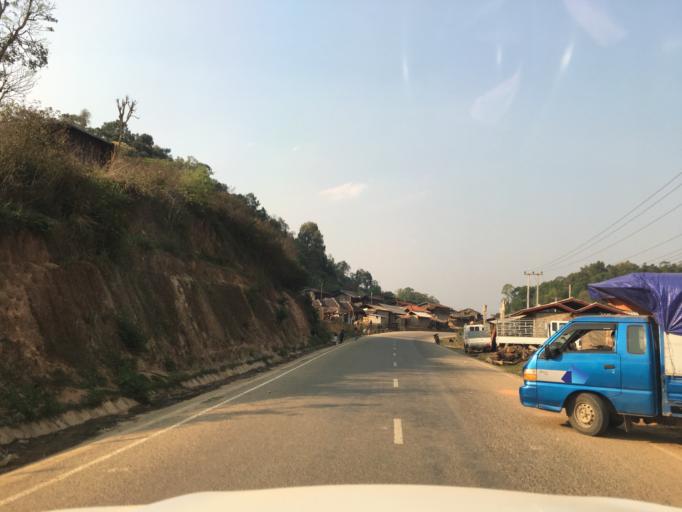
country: LA
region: Houaphan
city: Xam Nua
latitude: 20.5935
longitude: 104.0673
